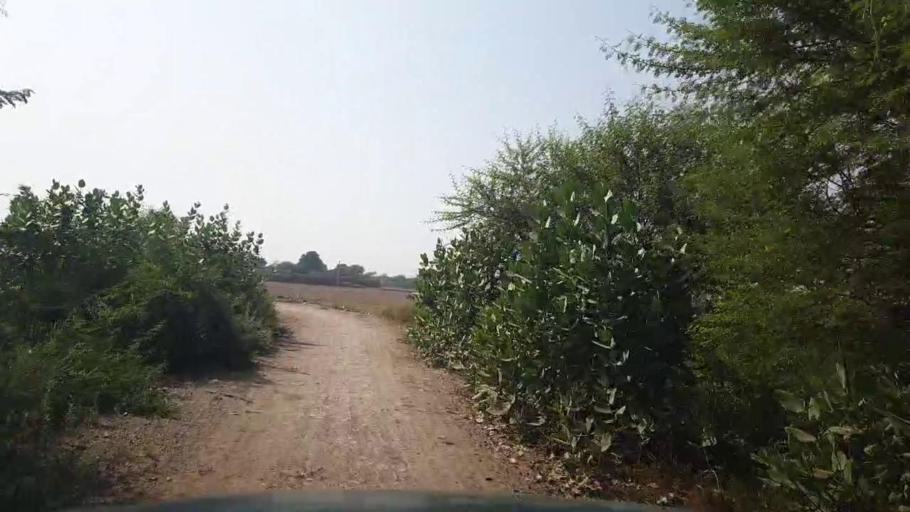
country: PK
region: Sindh
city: Bhit Shah
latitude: 25.7312
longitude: 68.4973
